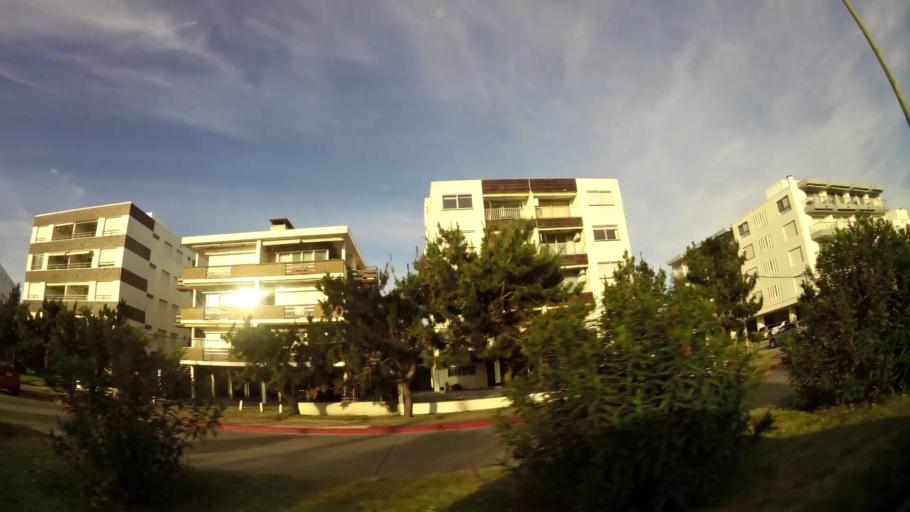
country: UY
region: Maldonado
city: Punta del Este
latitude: -34.9418
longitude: -54.9459
